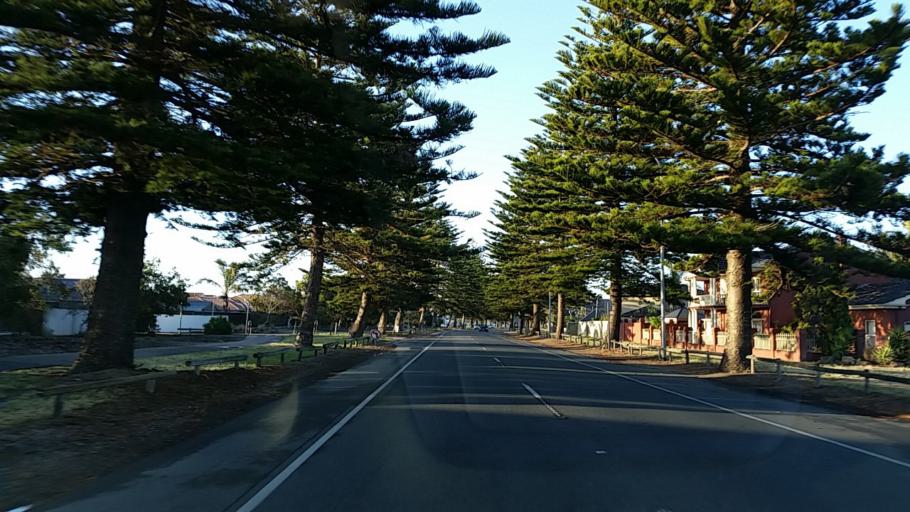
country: AU
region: South Australia
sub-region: Port Adelaide Enfield
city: Birkenhead
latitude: -34.7898
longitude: 138.4904
